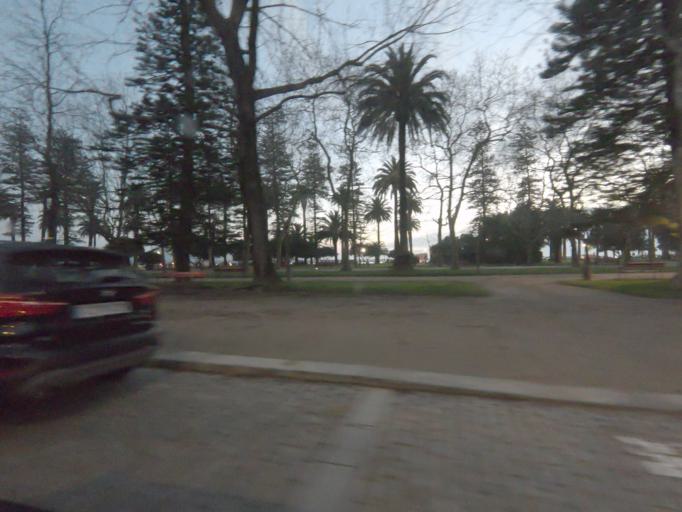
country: PT
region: Porto
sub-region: Vila Nova de Gaia
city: Canidelo
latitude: 41.1485
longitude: -8.6699
